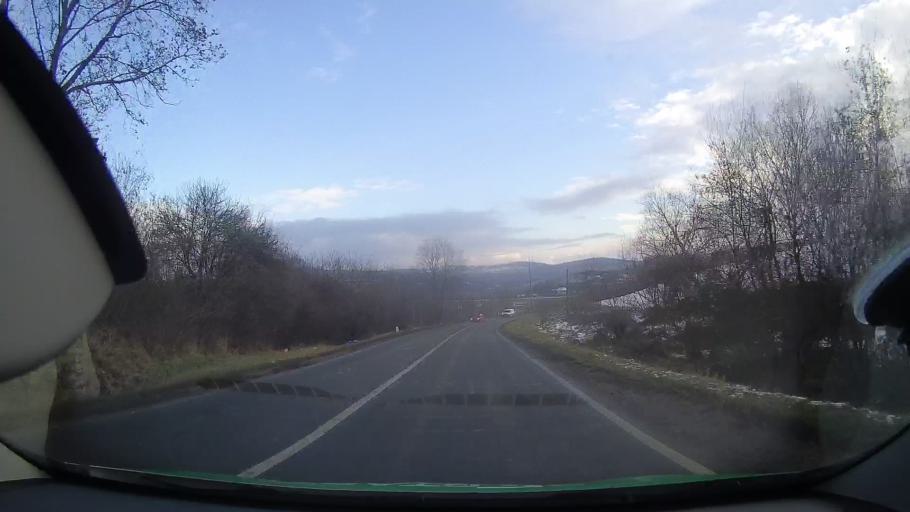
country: RO
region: Mures
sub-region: Comuna Cucerdea
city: Cucerdea
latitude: 46.4101
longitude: 24.2668
